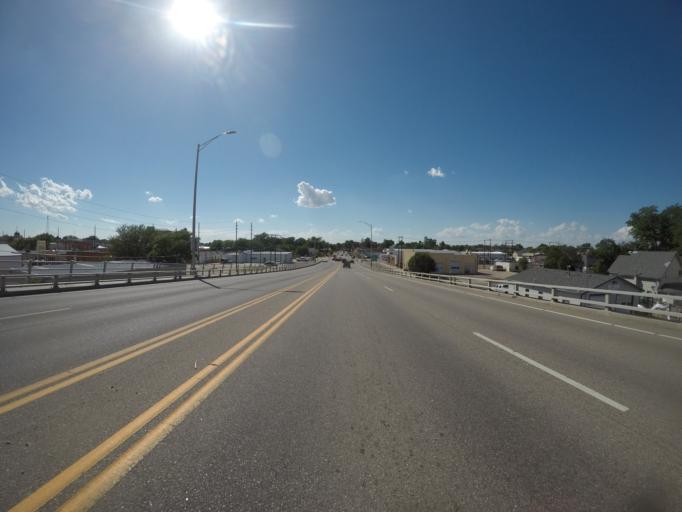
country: US
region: Colorado
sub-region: Logan County
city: Sterling
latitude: 40.6257
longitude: -103.2049
